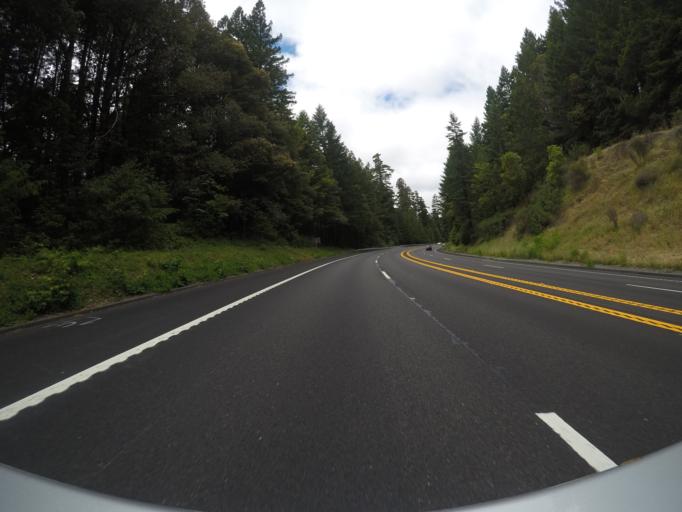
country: US
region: California
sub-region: Humboldt County
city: Redway
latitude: 40.3171
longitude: -123.9201
